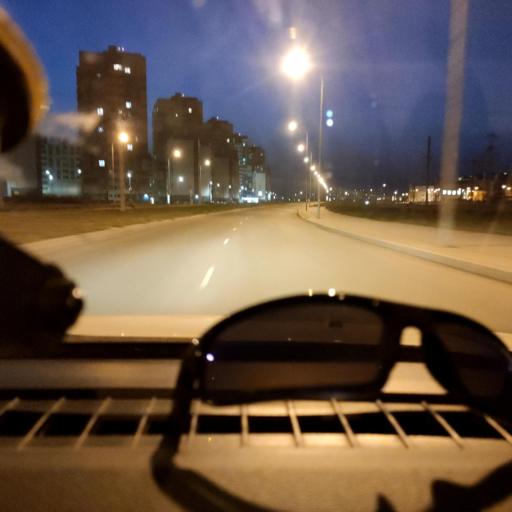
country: RU
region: Samara
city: Samara
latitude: 53.0962
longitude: 50.1710
